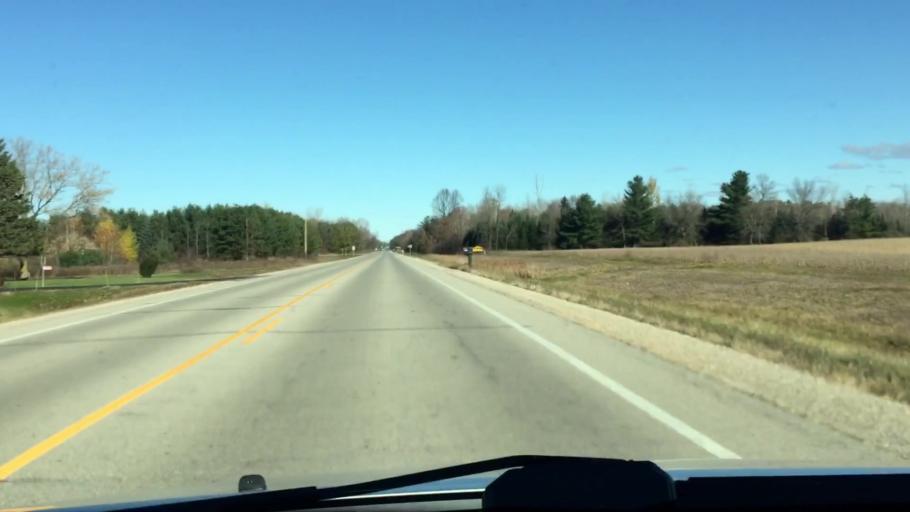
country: US
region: Wisconsin
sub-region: Brown County
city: Pulaski
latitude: 44.7502
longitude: -88.2495
